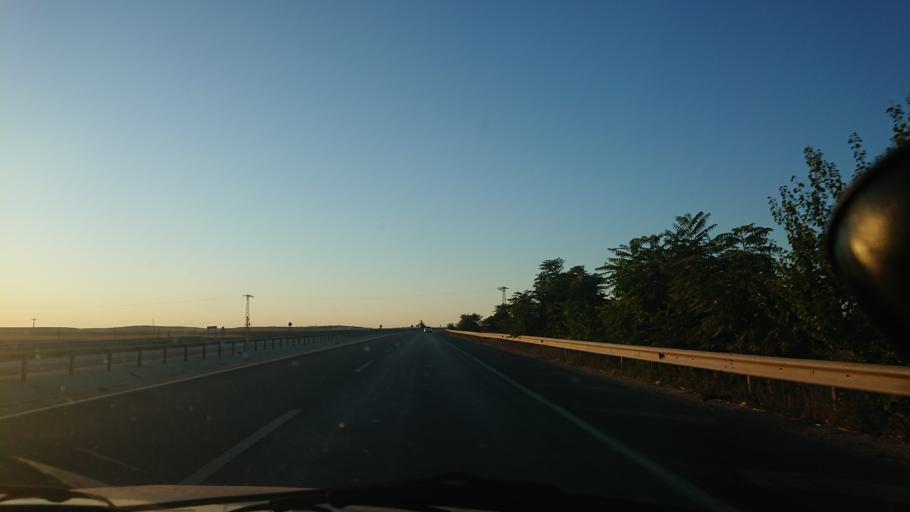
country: TR
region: Eskisehir
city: Mahmudiye
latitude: 39.5423
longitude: 30.9370
